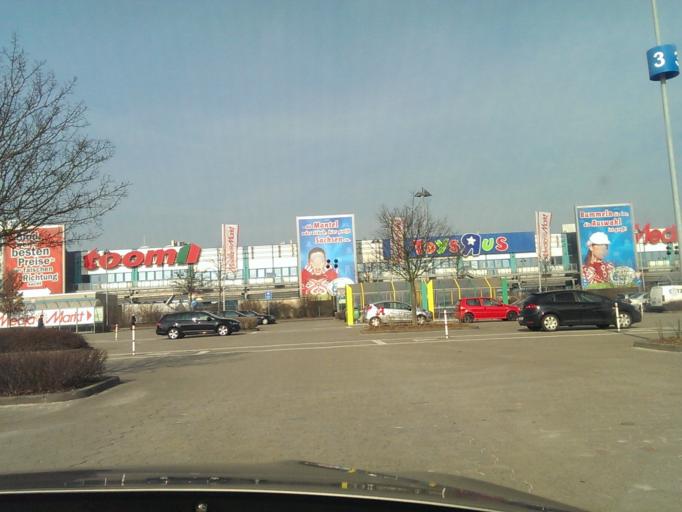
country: DE
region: Saxony
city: Wittgensdorf
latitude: 50.8640
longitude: 12.8685
